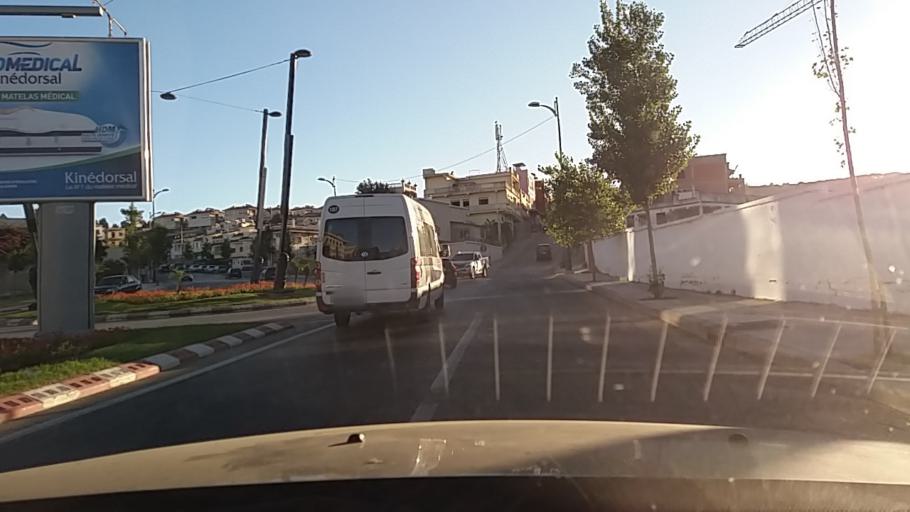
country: MA
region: Tanger-Tetouan
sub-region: Tanger-Assilah
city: Boukhalef
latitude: 35.7727
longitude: -5.8575
